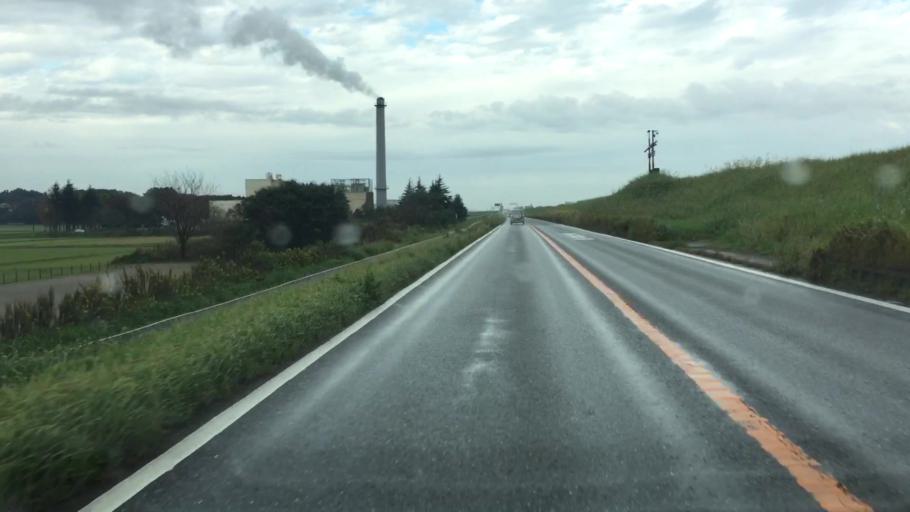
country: JP
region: Ibaraki
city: Toride
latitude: 35.8775
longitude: 140.0994
